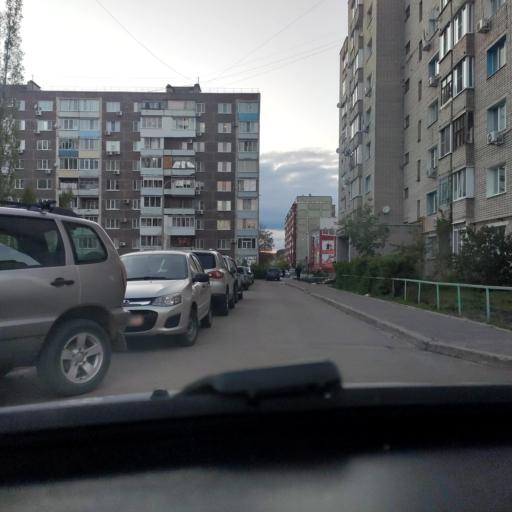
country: RU
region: Voronezj
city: Novovoronezh
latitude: 51.3184
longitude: 39.2050
